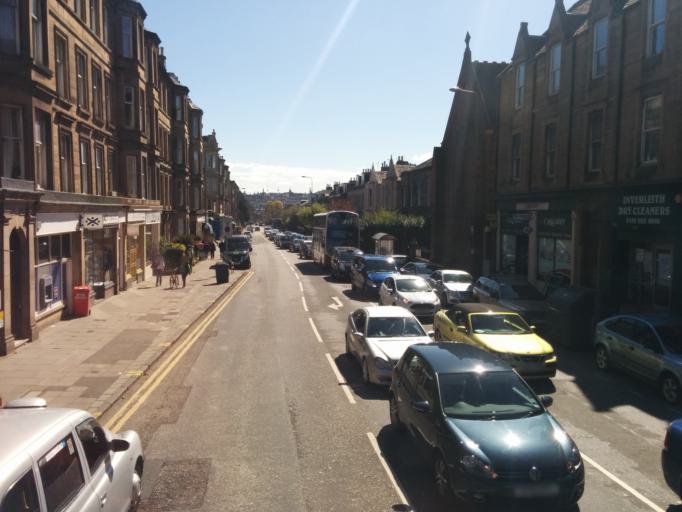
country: GB
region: Scotland
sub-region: Edinburgh
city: Edinburgh
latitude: 55.9709
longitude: -3.2090
